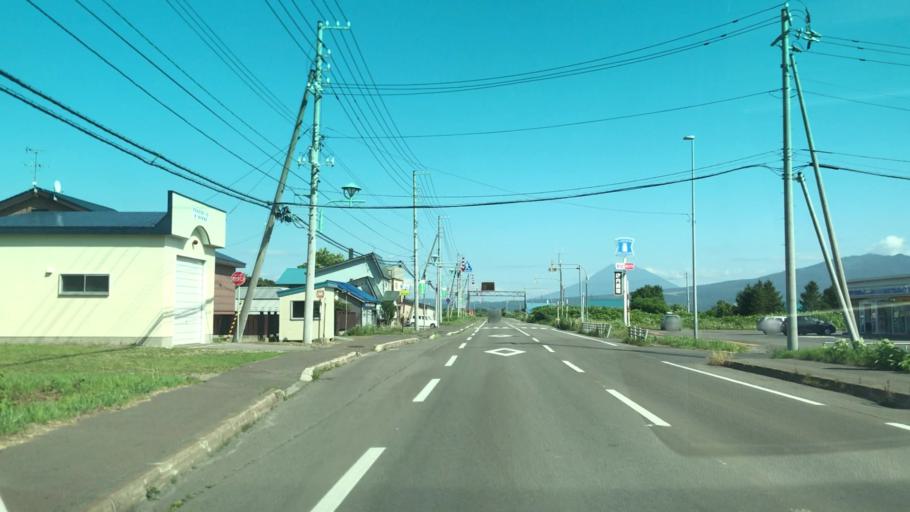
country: JP
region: Hokkaido
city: Iwanai
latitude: 43.0311
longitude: 140.5370
